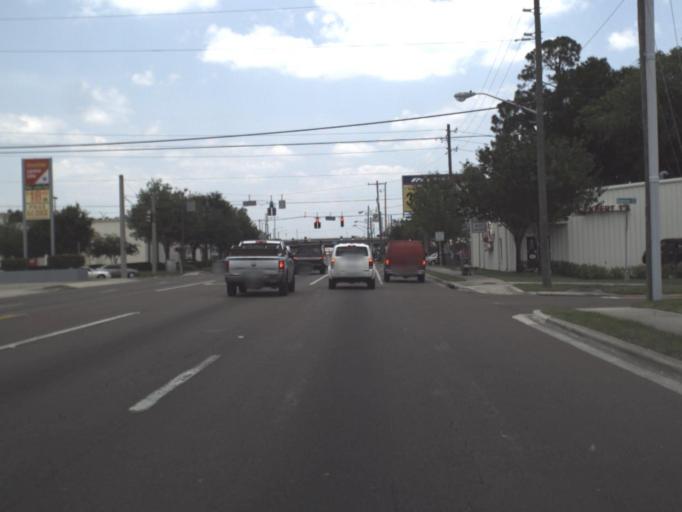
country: US
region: Florida
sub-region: Duval County
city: Jacksonville
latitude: 30.3143
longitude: -81.7306
